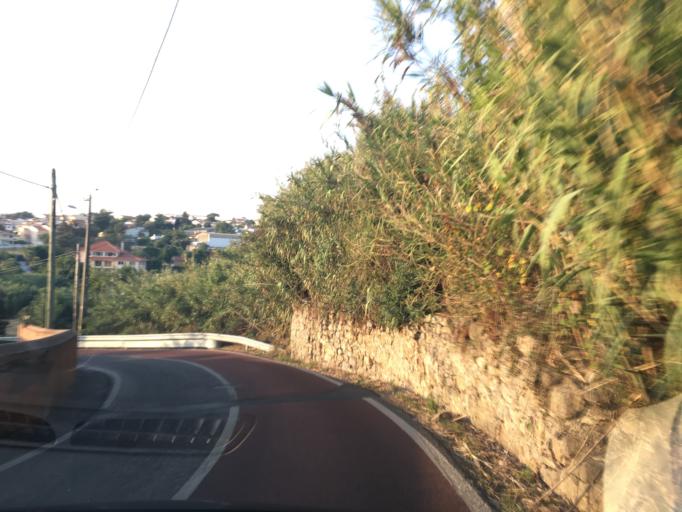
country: PT
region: Lisbon
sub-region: Sintra
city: Sintra
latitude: 38.8109
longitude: -9.3894
